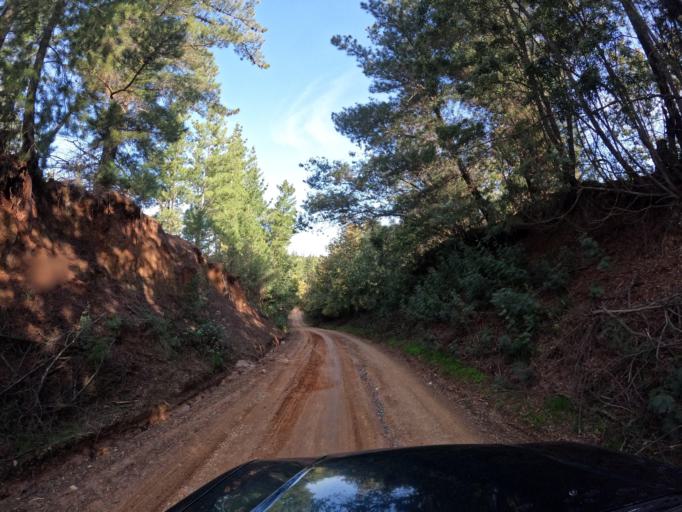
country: CL
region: Biobio
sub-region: Provincia de Biobio
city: La Laja
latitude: -37.1261
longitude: -72.7352
